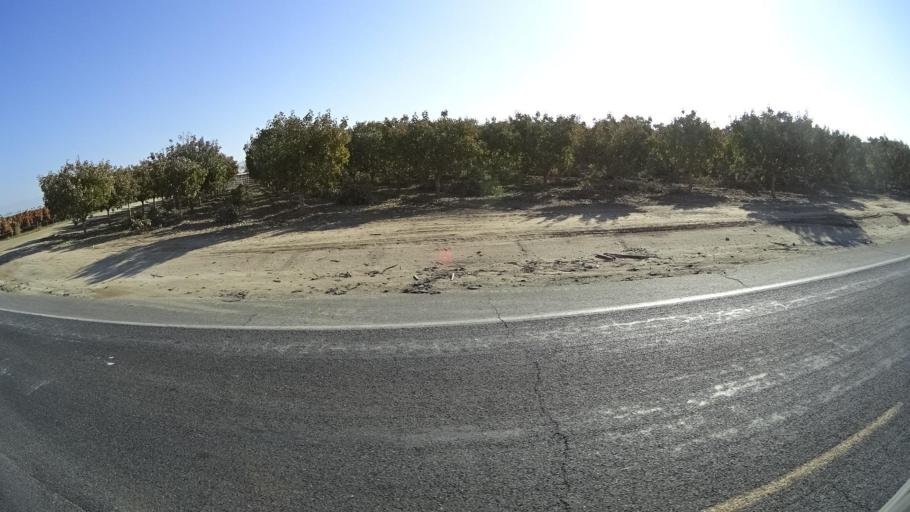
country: US
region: California
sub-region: Tulare County
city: Richgrove
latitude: 35.7507
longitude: -119.1395
